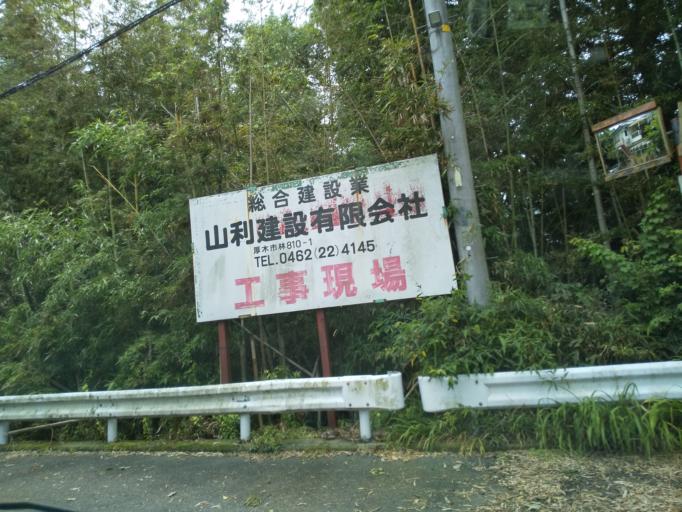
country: JP
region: Kanagawa
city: Zama
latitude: 35.5284
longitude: 139.3022
